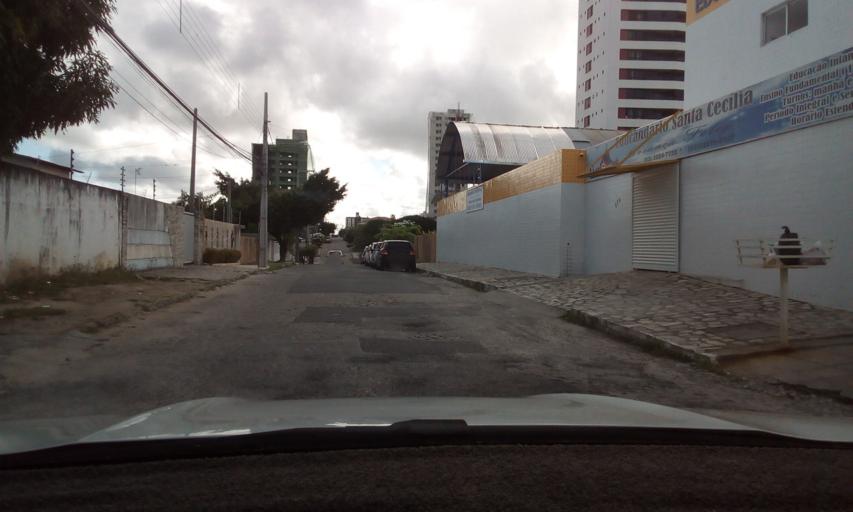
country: BR
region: Paraiba
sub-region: Joao Pessoa
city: Joao Pessoa
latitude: -7.1235
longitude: -34.8400
